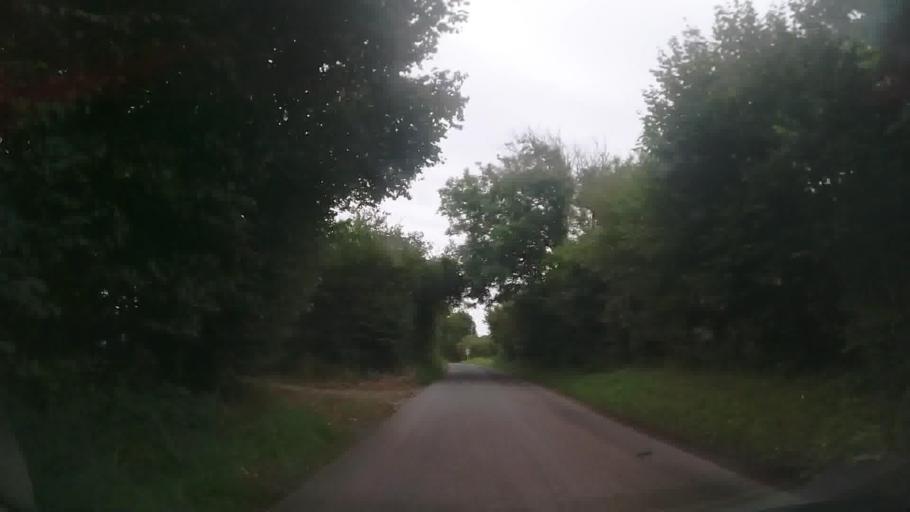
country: GB
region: Wales
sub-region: Carmarthenshire
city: Whitland
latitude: 51.7506
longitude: -4.5950
